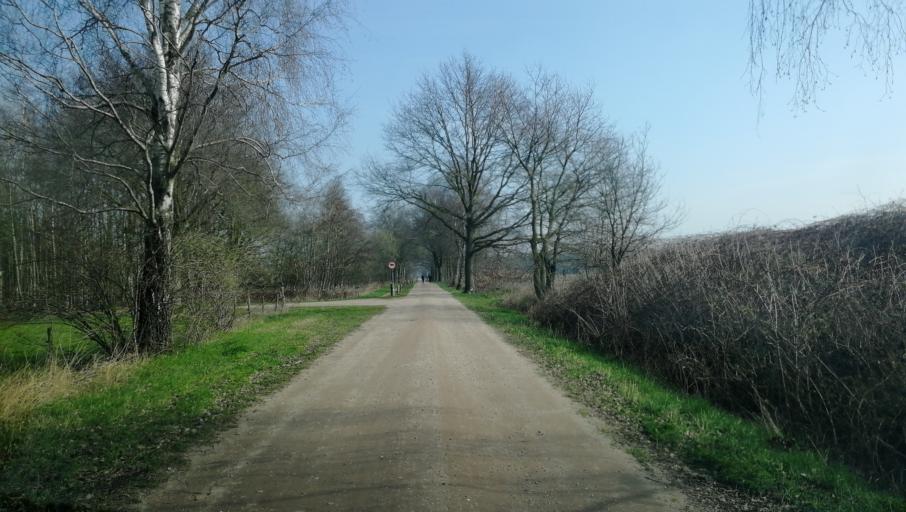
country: NL
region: Limburg
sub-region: Gemeente Peel en Maas
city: Maasbree
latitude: 51.4341
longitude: 6.0597
